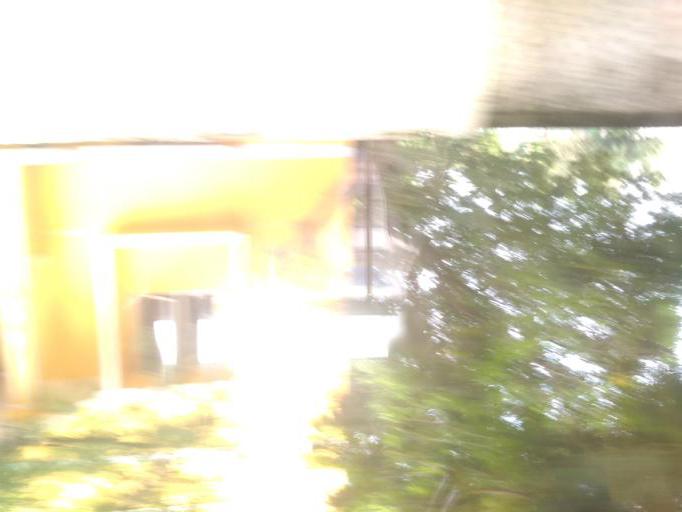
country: IN
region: Tamil Nadu
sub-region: Chennai
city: Gandhi Nagar
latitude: 13.0112
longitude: 80.2490
